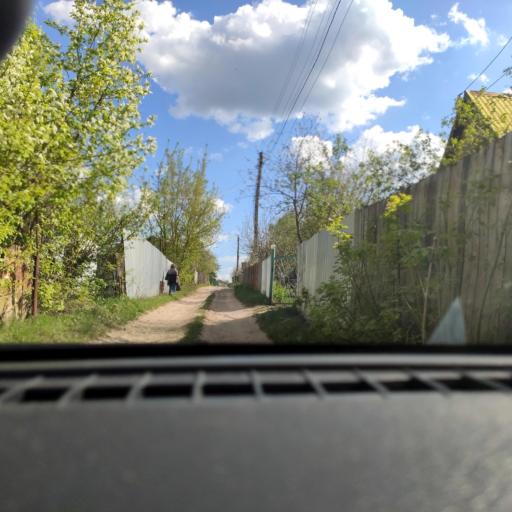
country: RU
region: Samara
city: Zhigulevsk
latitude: 53.3722
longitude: 49.5093
